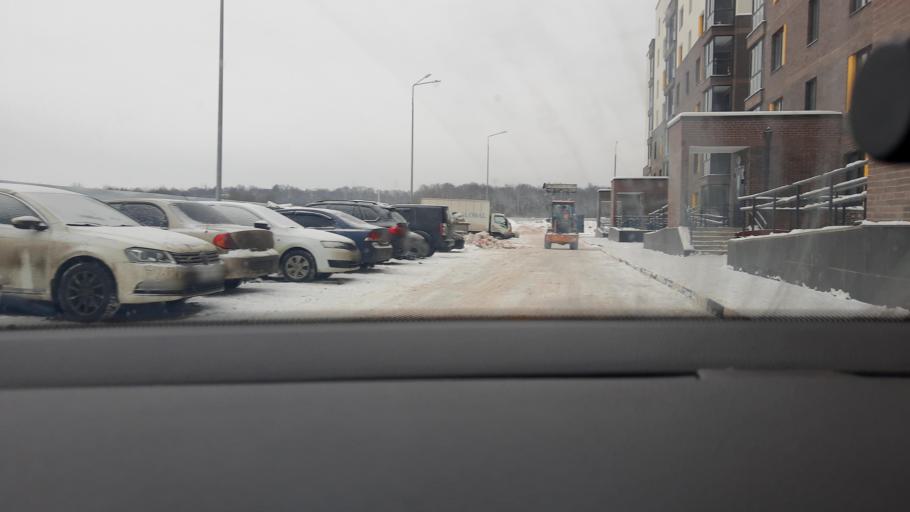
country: RU
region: Moskovskaya
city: Pirogovskiy
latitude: 55.9592
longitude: 37.6826
